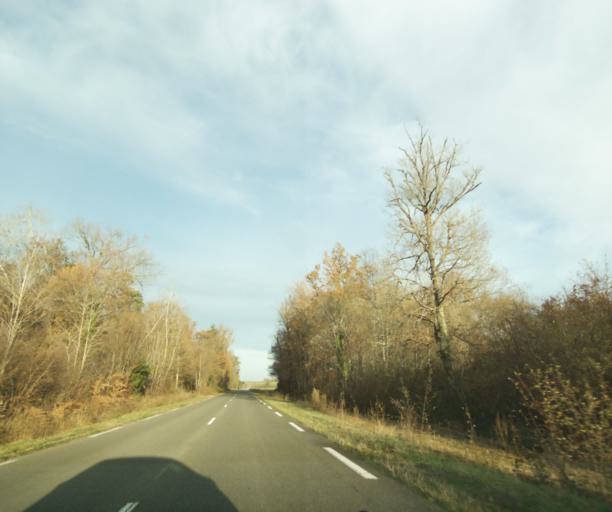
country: FR
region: Aquitaine
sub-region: Departement des Landes
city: Gabarret
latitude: 43.9595
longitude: -0.0152
